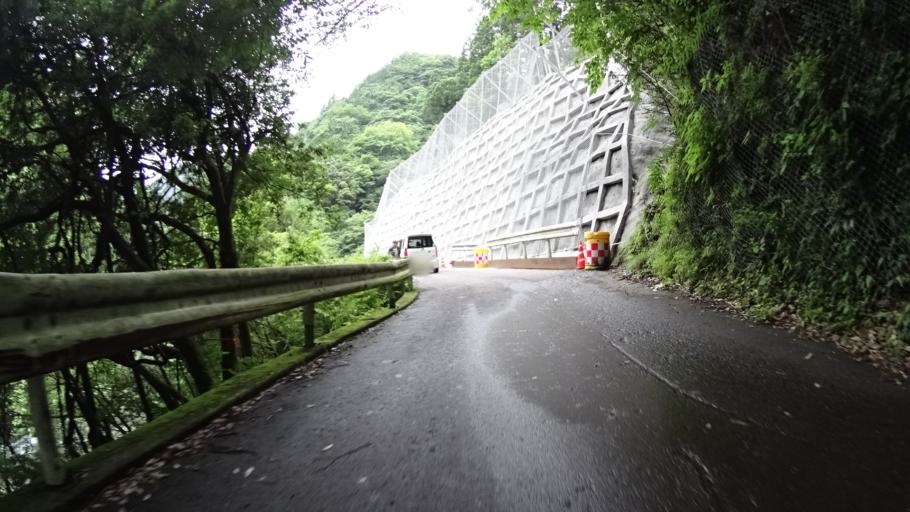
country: JP
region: Kanagawa
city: Hadano
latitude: 35.4844
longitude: 139.2058
